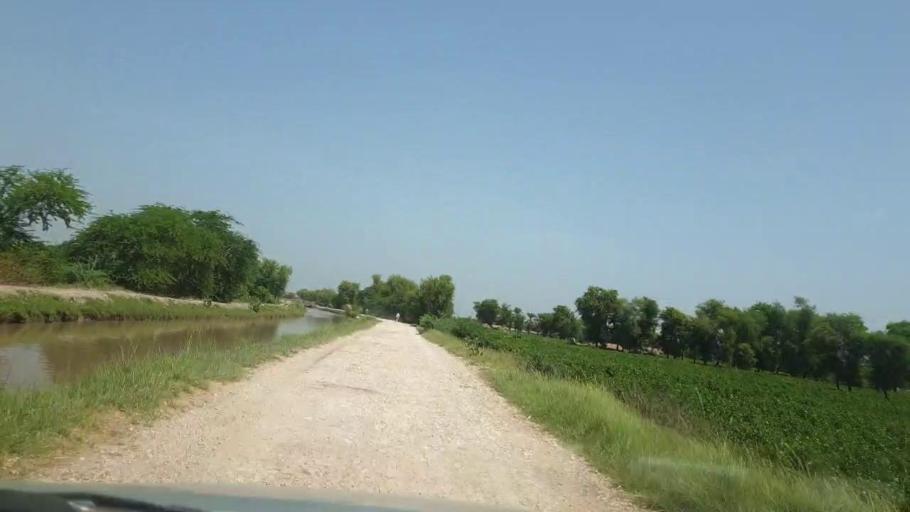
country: PK
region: Sindh
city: Pano Aqil
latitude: 27.6480
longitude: 69.1055
